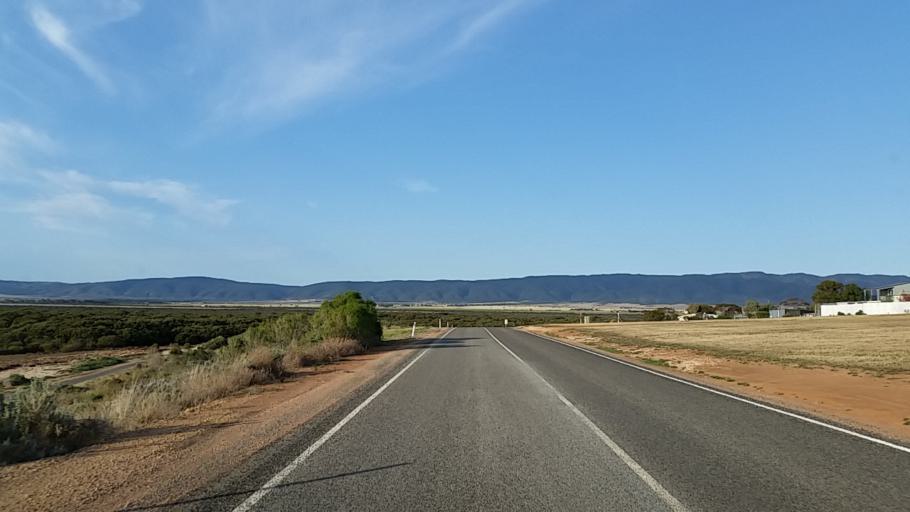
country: AU
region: South Australia
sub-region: Port Pirie City and Dists
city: Port Pirie
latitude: -33.1001
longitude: 138.0289
